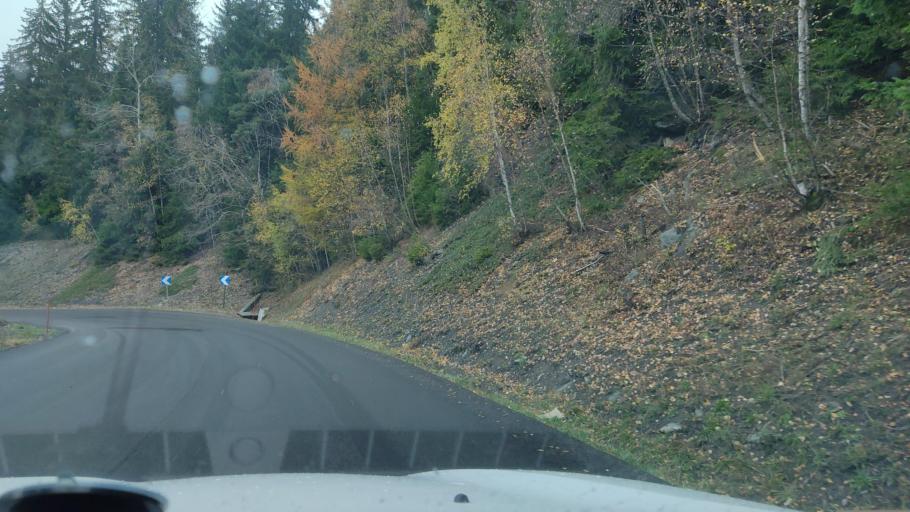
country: FR
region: Rhone-Alpes
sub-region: Departement de la Savoie
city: Bourg-Saint-Maurice
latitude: 45.5877
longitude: 6.7805
